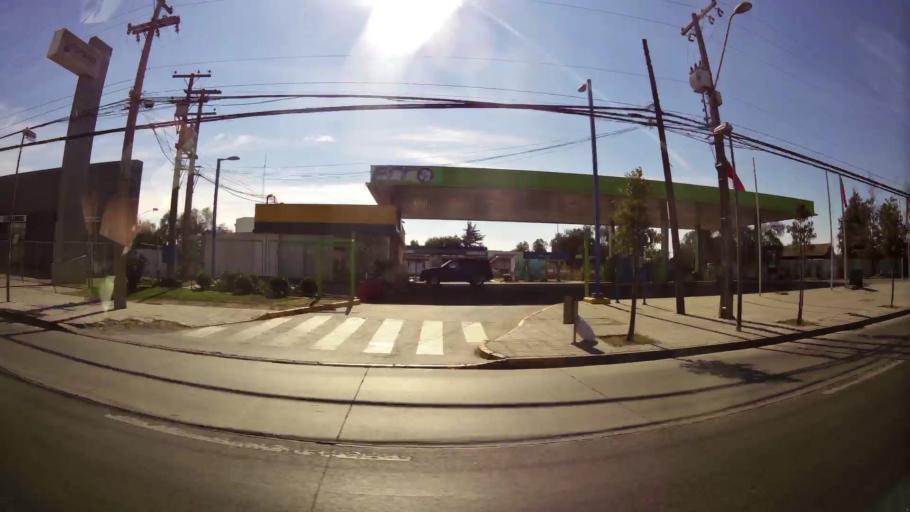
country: CL
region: Santiago Metropolitan
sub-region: Provincia de Santiago
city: Lo Prado
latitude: -33.4861
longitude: -70.6984
